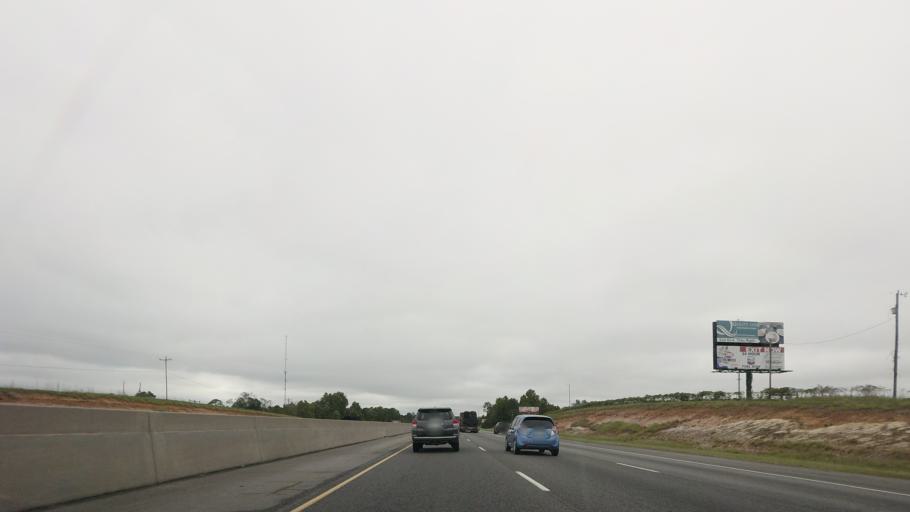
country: US
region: Georgia
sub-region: Turner County
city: Ashburn
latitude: 31.7462
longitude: -83.6597
